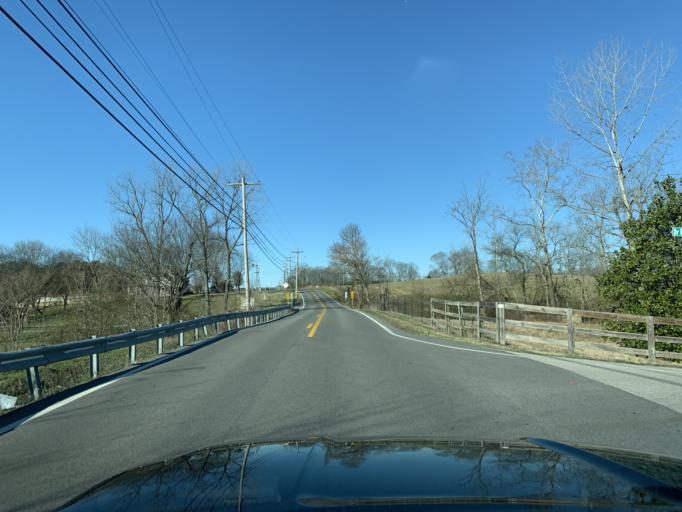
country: US
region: Tennessee
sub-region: Maury County
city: Spring Hill
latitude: 35.7529
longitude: -86.9756
